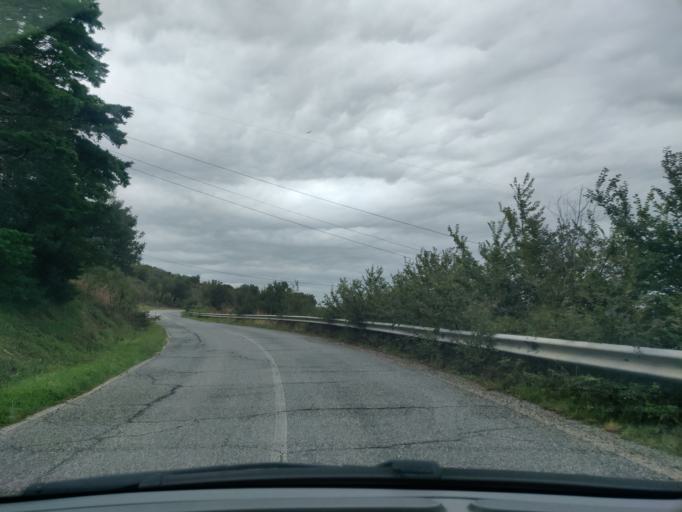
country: IT
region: Latium
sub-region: Citta metropolitana di Roma Capitale
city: Aurelia
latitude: 42.1326
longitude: 11.8409
